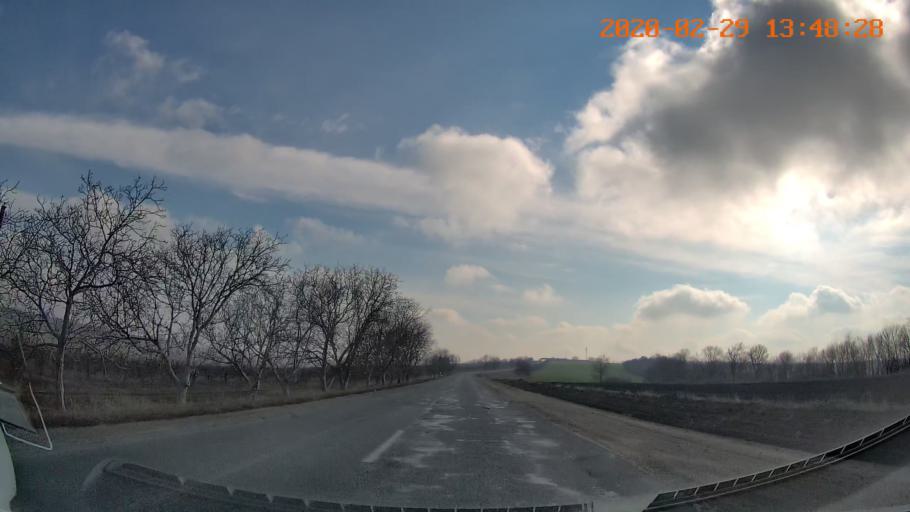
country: MD
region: Floresti
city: Leninskiy
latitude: 47.8540
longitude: 28.4860
